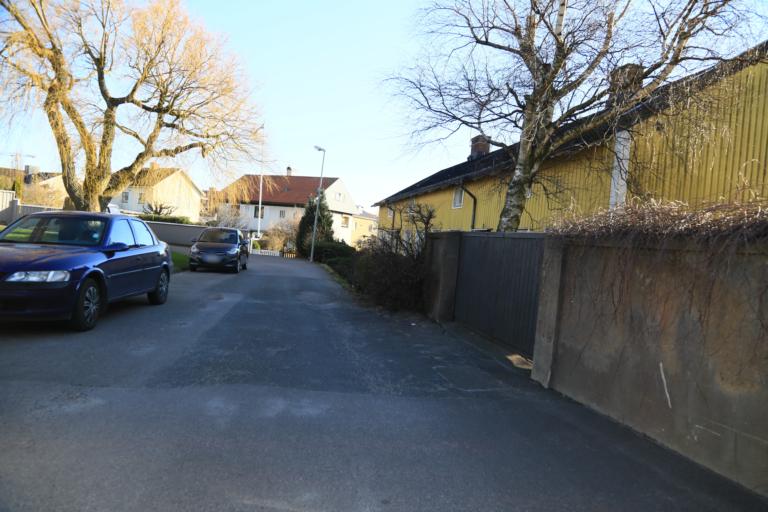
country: SE
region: Halland
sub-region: Varbergs Kommun
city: Varberg
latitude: 57.1023
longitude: 12.2475
